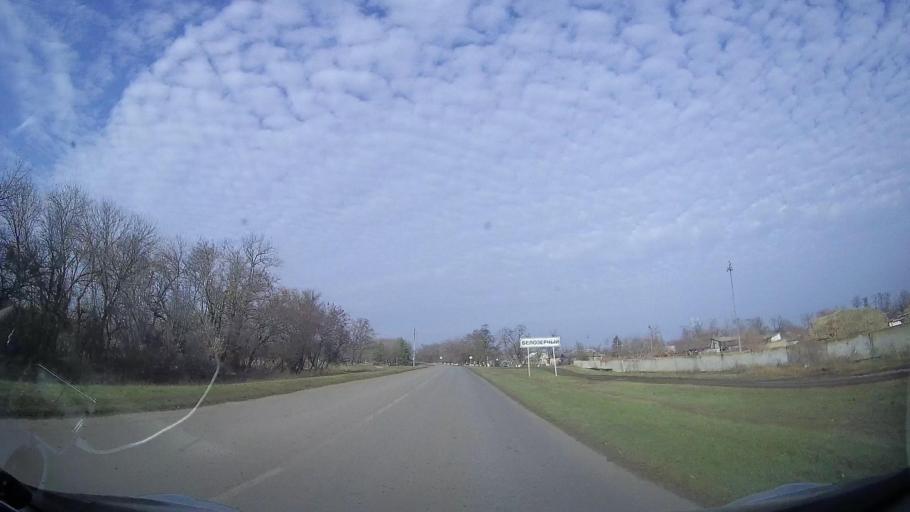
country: RU
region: Rostov
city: Gigant
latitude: 46.8343
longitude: 41.3344
